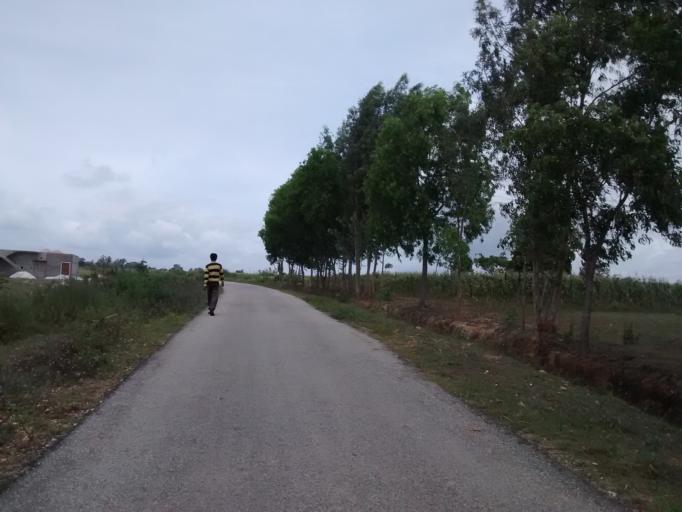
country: IN
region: Karnataka
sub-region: Hassan
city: Hassan
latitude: 12.9253
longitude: 76.1370
